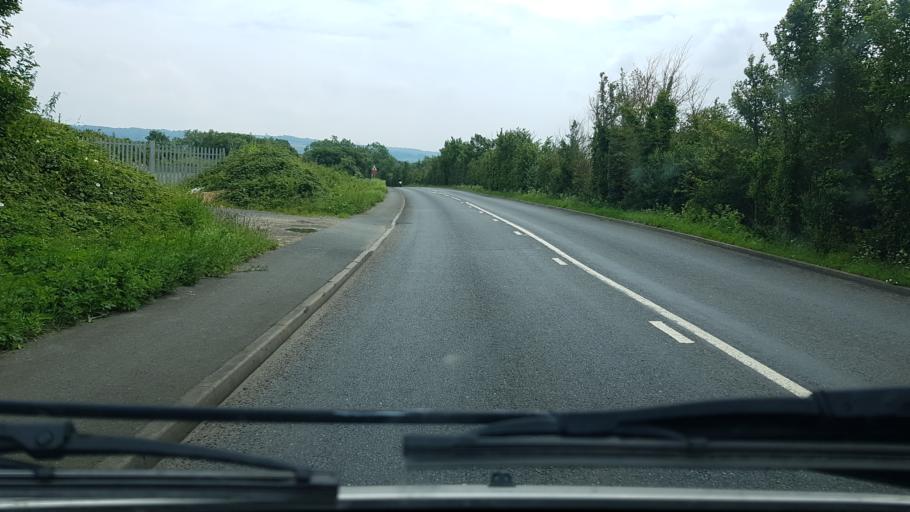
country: GB
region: England
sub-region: Worcestershire
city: Badsey
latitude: 52.0558
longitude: -1.8852
